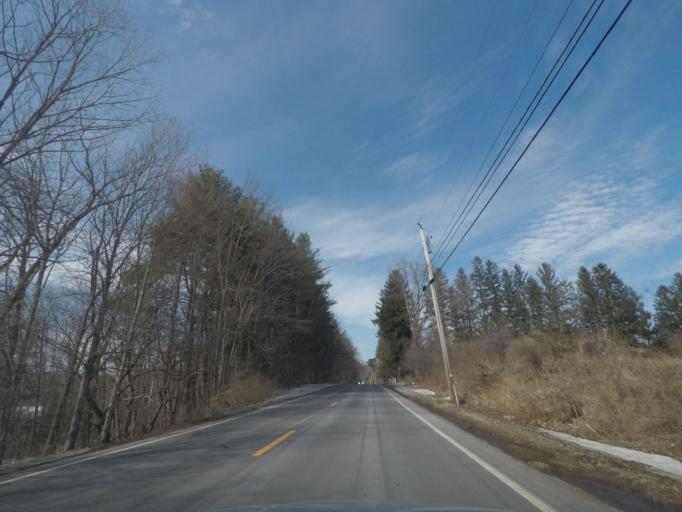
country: US
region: Massachusetts
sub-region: Berkshire County
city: West Stockbridge
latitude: 42.3461
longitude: -73.3796
